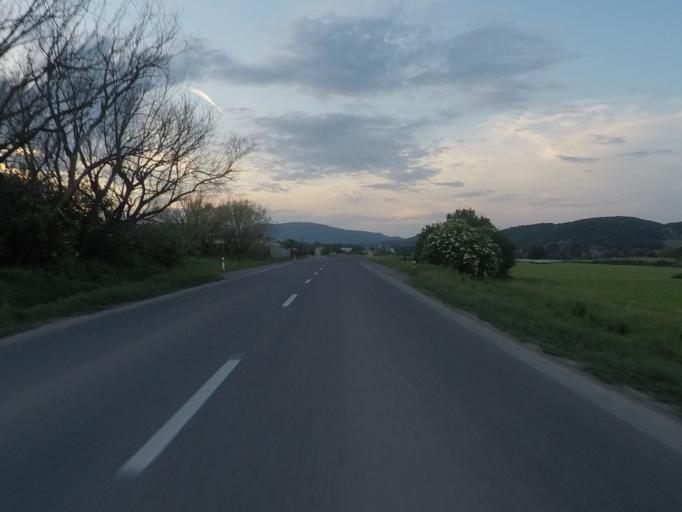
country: SK
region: Banskobystricky
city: Rimavska Sobota
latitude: 48.4571
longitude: 19.9537
